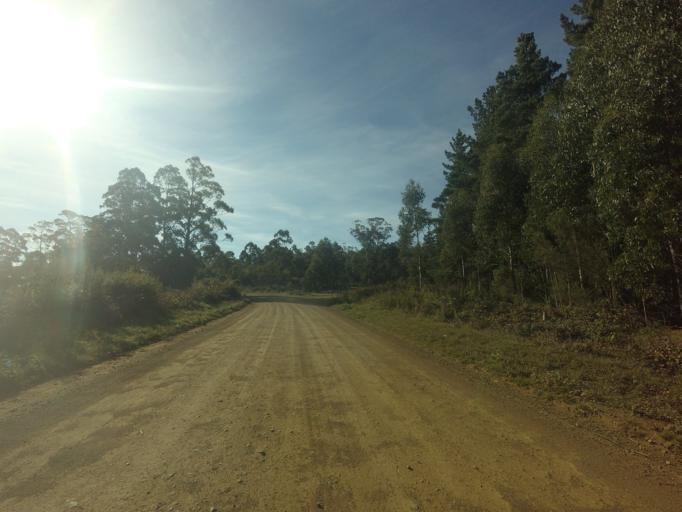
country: AU
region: Tasmania
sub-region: Sorell
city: Sorell
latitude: -42.4857
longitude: 147.4905
